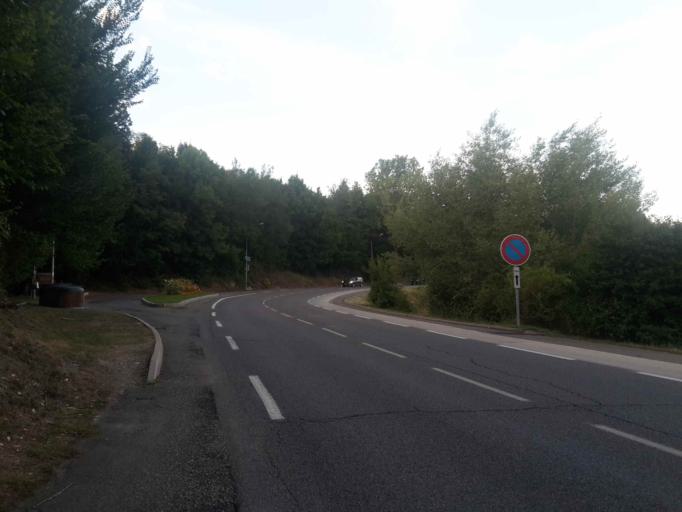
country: FR
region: Provence-Alpes-Cote d'Azur
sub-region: Departement des Hautes-Alpes
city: Embrun
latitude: 44.5584
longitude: 6.4843
